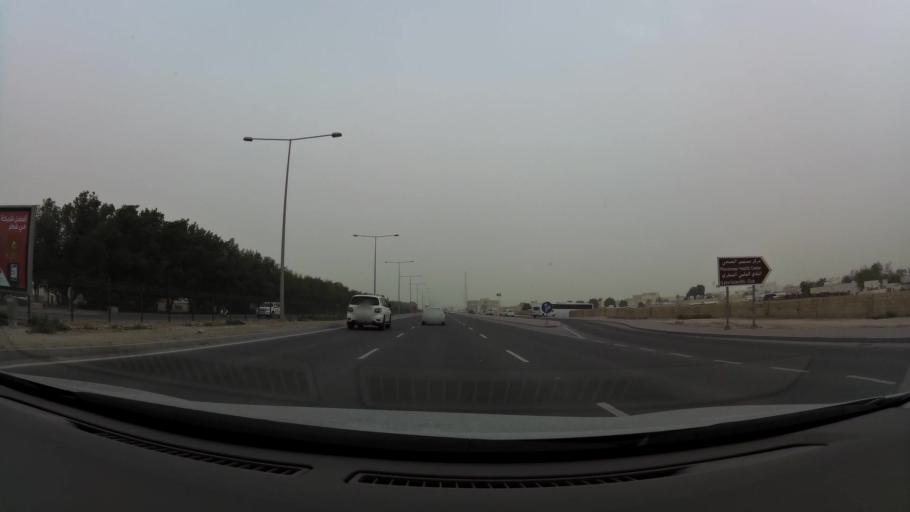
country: QA
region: Baladiyat ad Dawhah
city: Doha
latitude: 25.2368
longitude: 51.4815
